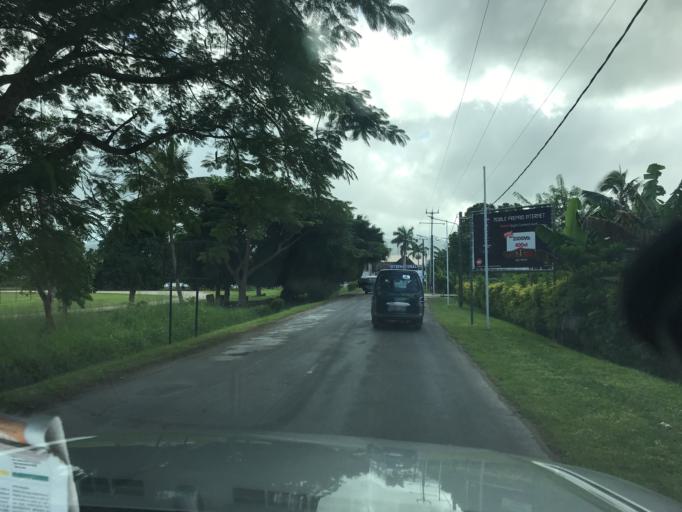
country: VU
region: Shefa
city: Port-Vila
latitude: -17.7030
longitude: 168.3187
